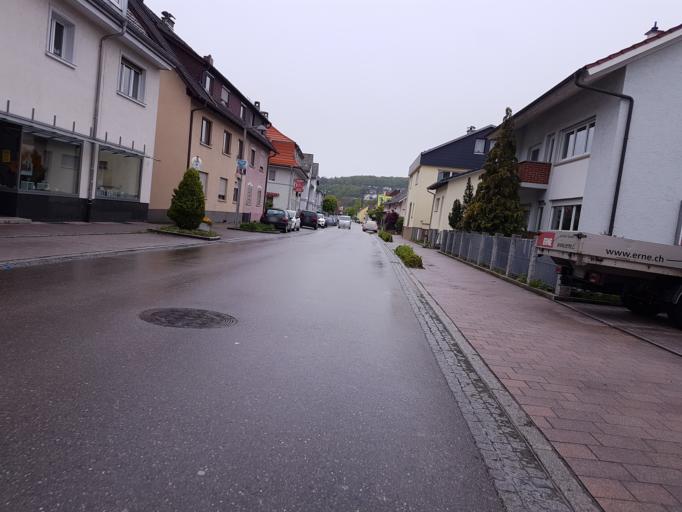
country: DE
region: Baden-Wuerttemberg
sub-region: Freiburg Region
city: Lauchringen
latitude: 47.6301
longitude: 8.3012
